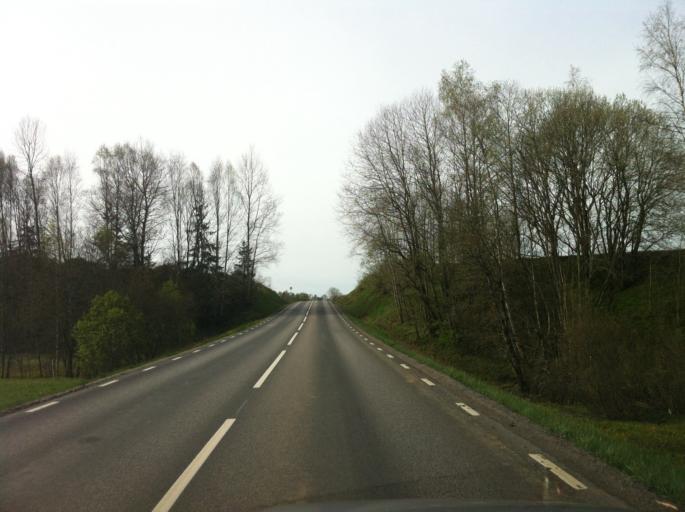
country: SE
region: Vaestra Goetaland
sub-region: Bollebygds Kommun
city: Bollebygd
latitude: 57.6896
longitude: 12.5691
